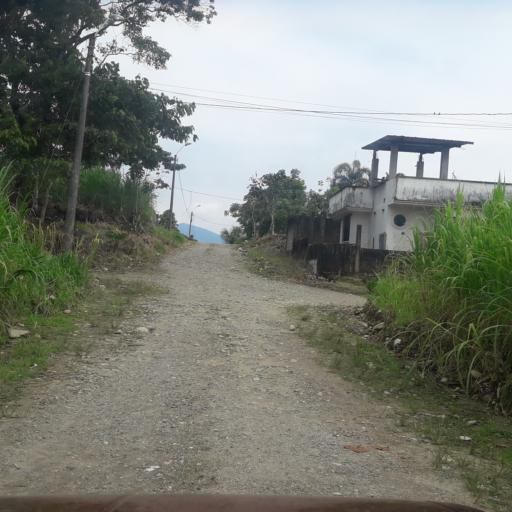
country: EC
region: Napo
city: Tena
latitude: -0.9805
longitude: -77.8159
